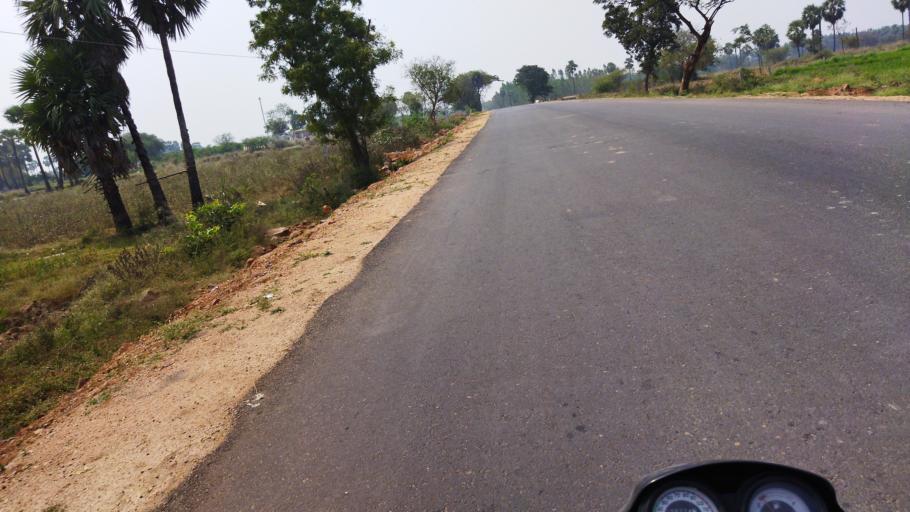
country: IN
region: Telangana
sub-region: Nalgonda
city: Nalgonda
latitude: 17.1552
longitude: 79.4113
